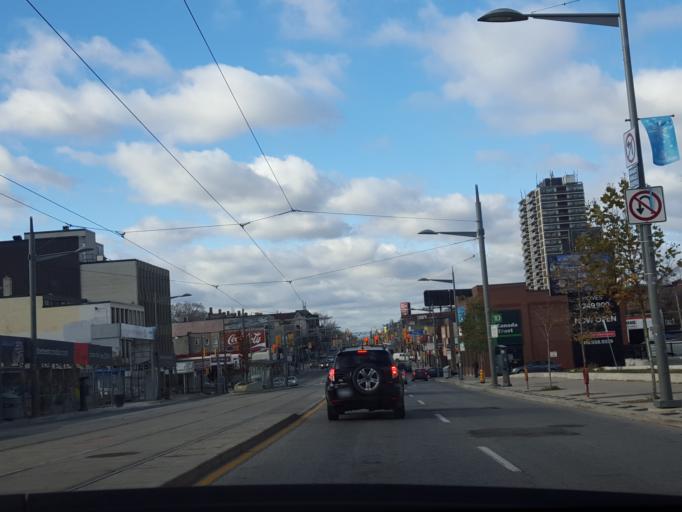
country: CA
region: Ontario
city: Toronto
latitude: 43.6806
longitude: -79.4311
